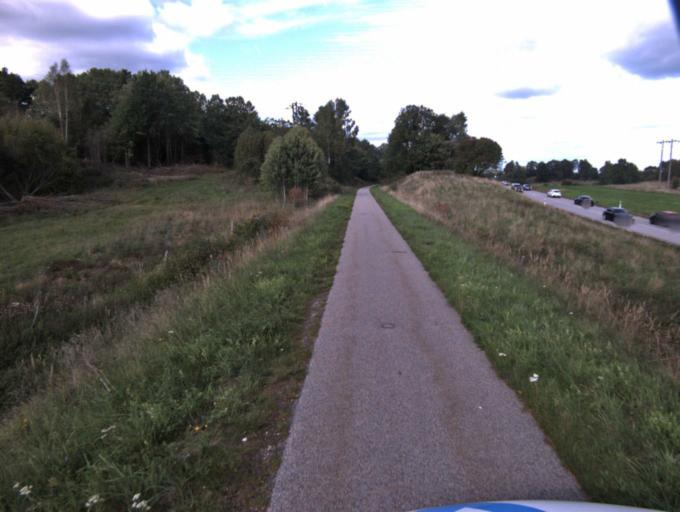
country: SE
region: Vaestra Goetaland
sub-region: Ulricehamns Kommun
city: Ulricehamn
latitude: 57.8855
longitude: 13.4329
